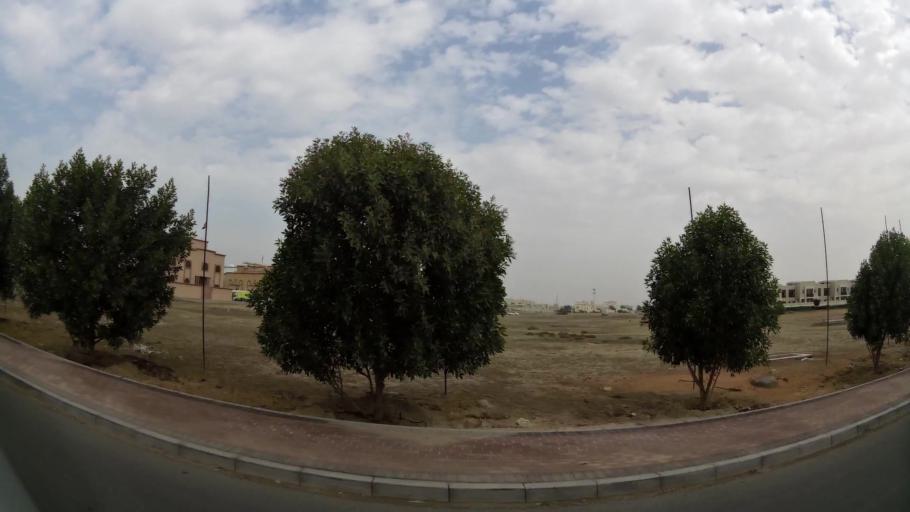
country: AE
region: Abu Dhabi
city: Abu Dhabi
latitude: 24.3150
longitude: 54.6173
